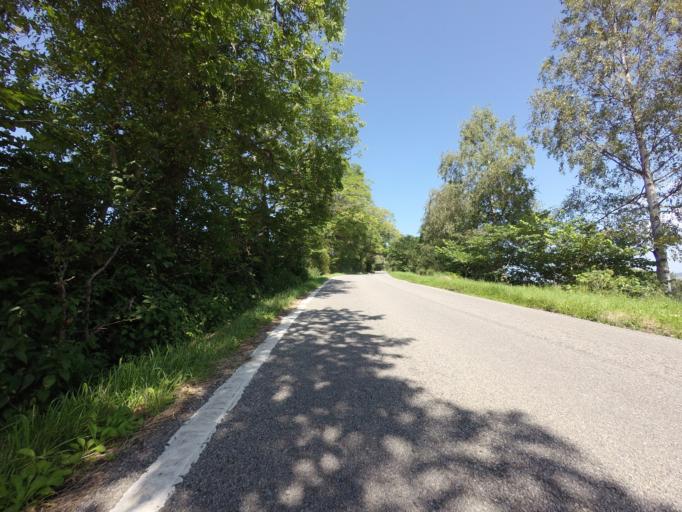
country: GB
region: Scotland
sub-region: Highland
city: Dingwall
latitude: 57.6125
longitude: -4.4146
